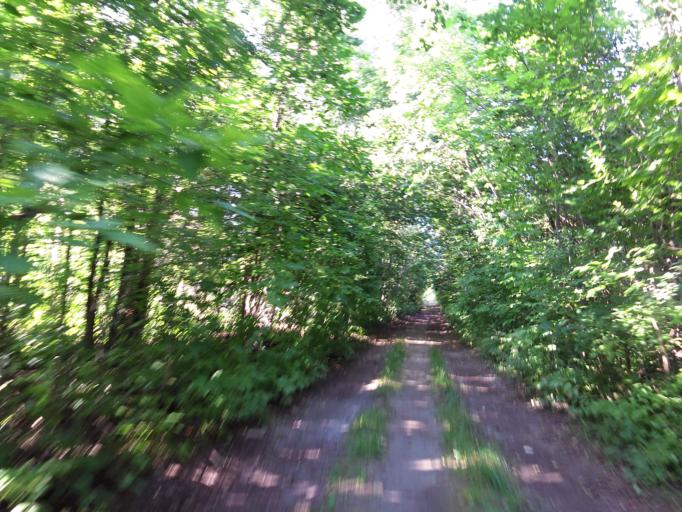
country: CA
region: Ontario
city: Ottawa
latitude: 45.4249
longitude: -75.7413
